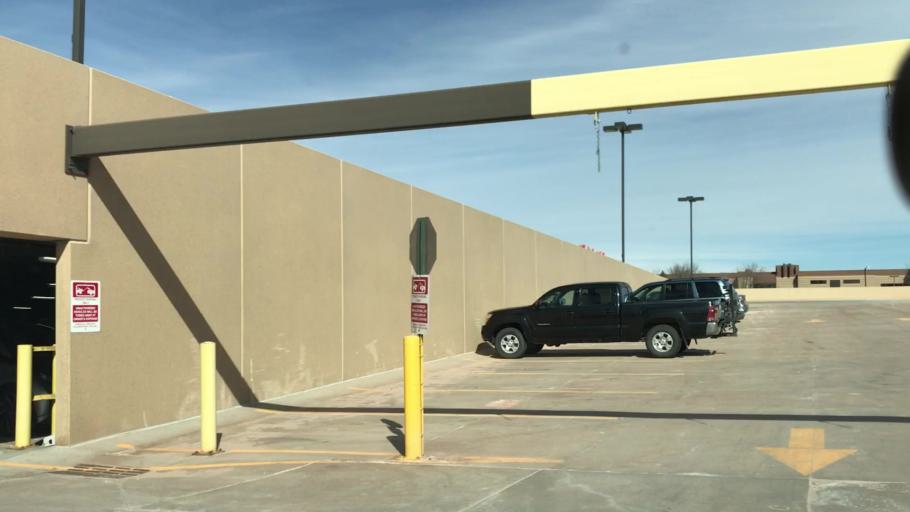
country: US
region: Colorado
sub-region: Boulder County
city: Gunbarrel
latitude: 40.0631
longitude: -105.2117
